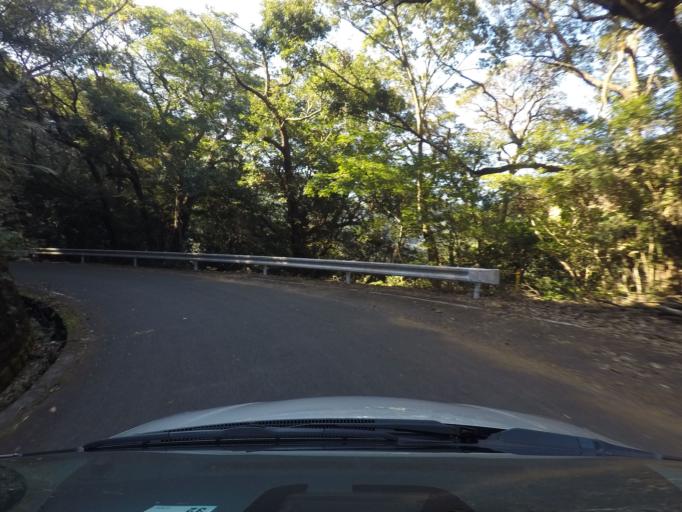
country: JP
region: Miyazaki
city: Kobayashi
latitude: 32.0232
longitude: 131.1869
